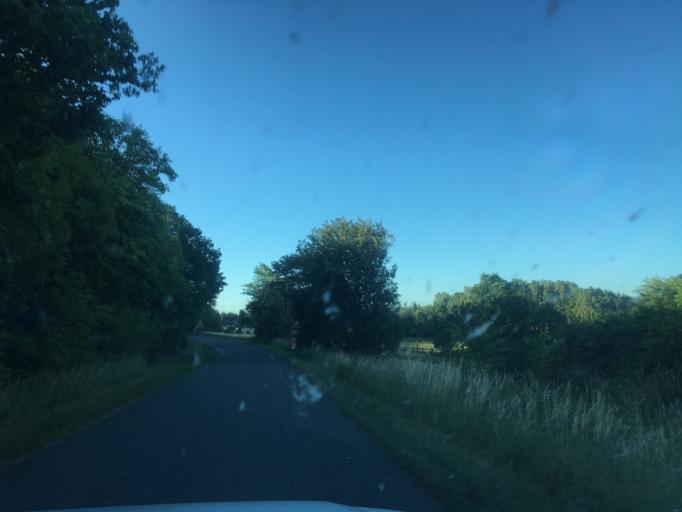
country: DK
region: Central Jutland
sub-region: Randers Kommune
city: Langa
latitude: 56.3903
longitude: 9.8608
